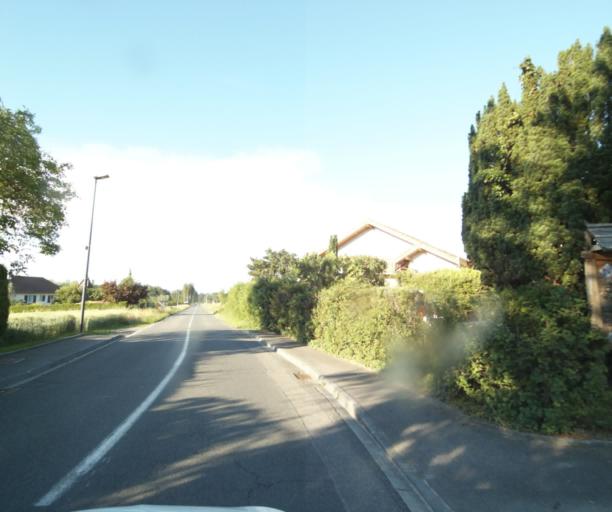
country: FR
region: Rhone-Alpes
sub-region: Departement de la Haute-Savoie
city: Messery
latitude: 46.3526
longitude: 6.2997
